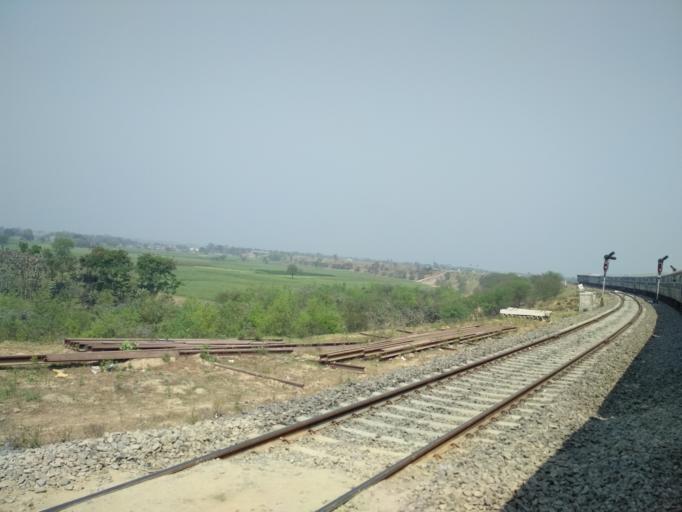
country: IN
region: Bihar
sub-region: Munger
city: Munger
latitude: 25.4277
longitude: 86.4376
